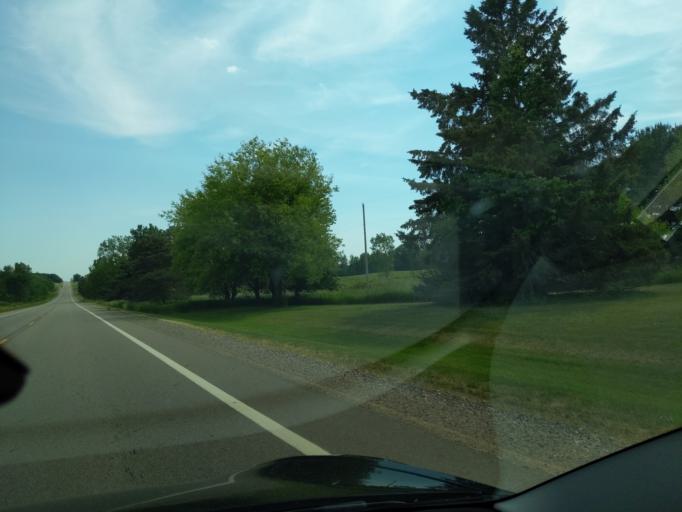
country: US
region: Michigan
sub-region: Barry County
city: Nashville
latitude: 42.6465
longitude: -85.0950
